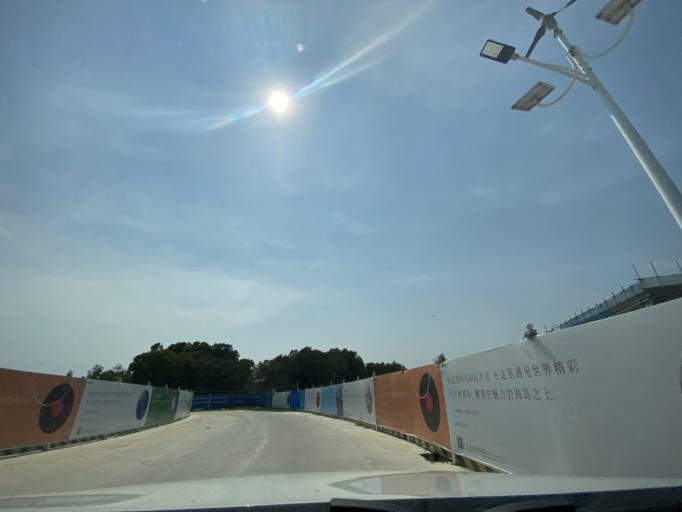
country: CN
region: Hainan
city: Yingzhou
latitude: 18.4093
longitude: 109.8363
